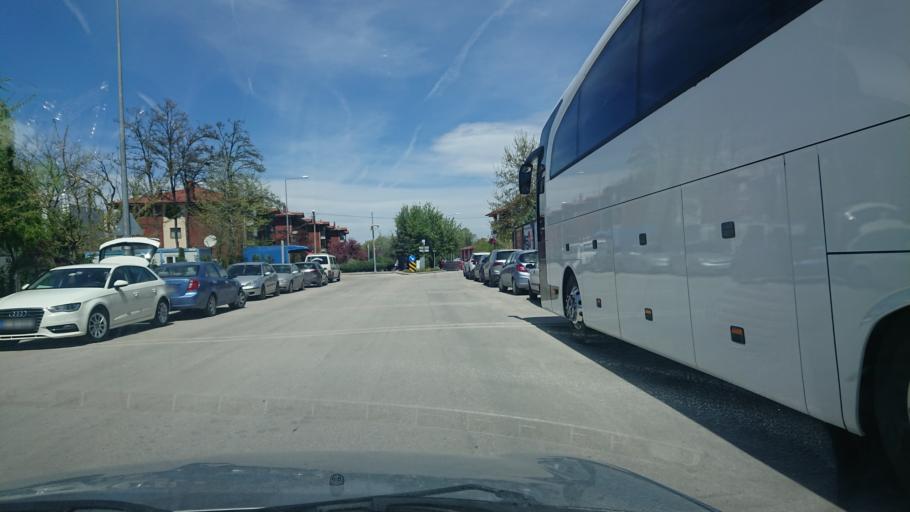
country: TR
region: Eskisehir
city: Eskisehir
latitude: 39.7663
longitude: 30.4970
